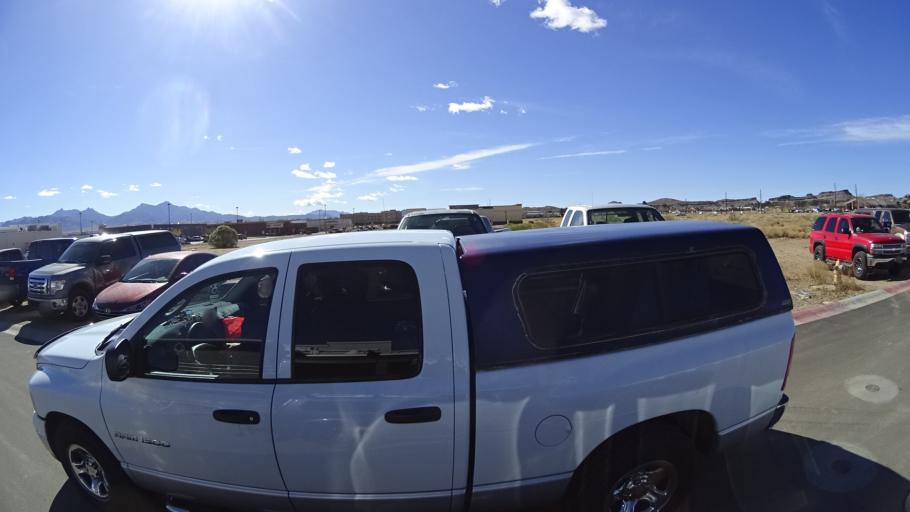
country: US
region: Arizona
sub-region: Mohave County
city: New Kingman-Butler
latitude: 35.2269
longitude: -114.0381
